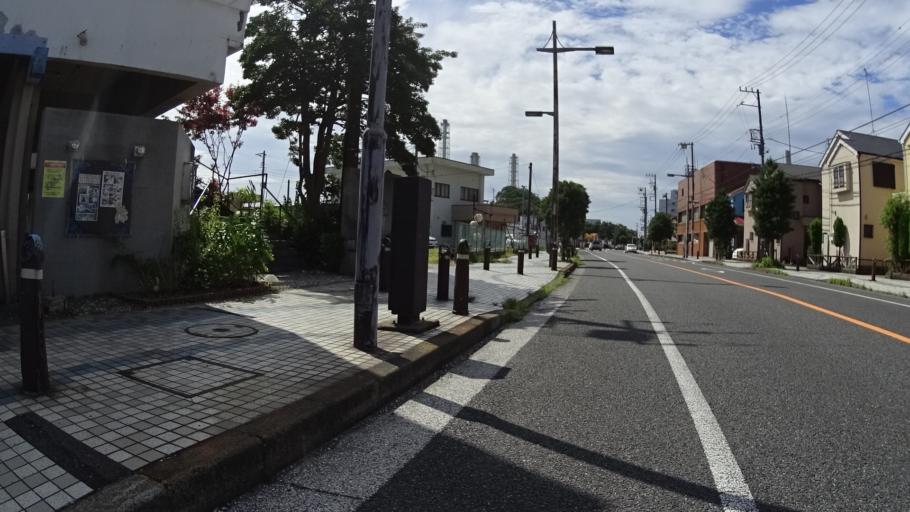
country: JP
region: Kanagawa
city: Yokosuka
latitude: 35.2213
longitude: 139.7123
